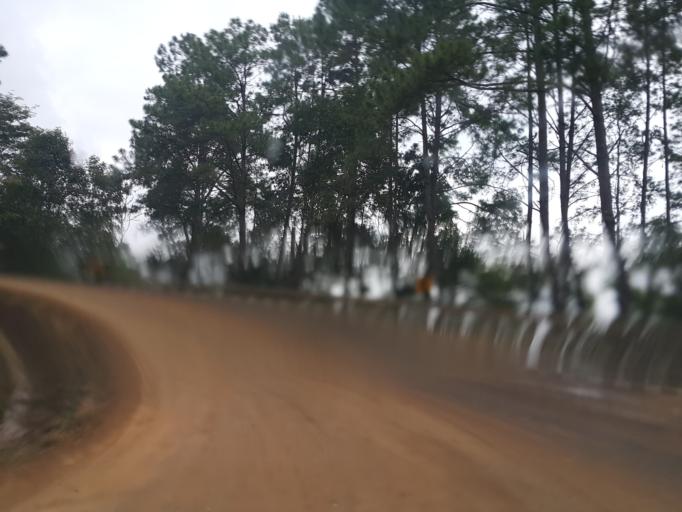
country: TH
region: Mae Hong Son
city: Mae Hi
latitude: 19.2687
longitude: 98.5809
